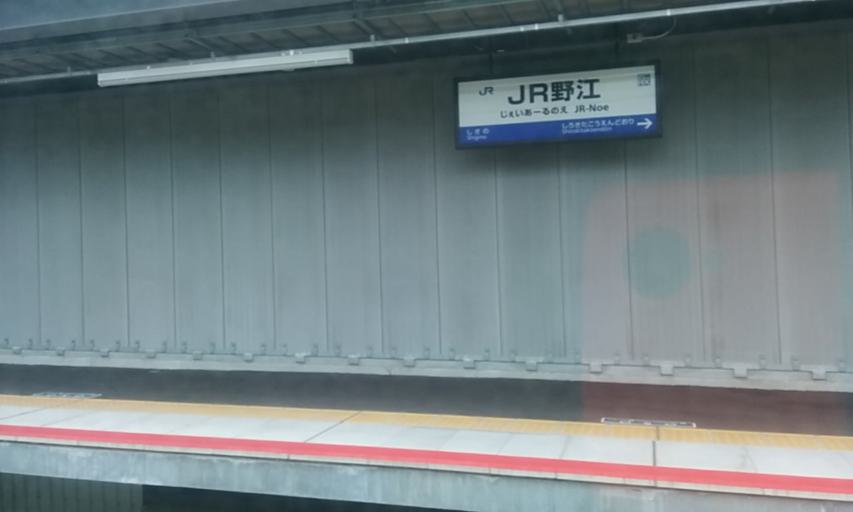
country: JP
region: Osaka
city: Moriguchi
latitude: 34.7066
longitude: 135.5413
